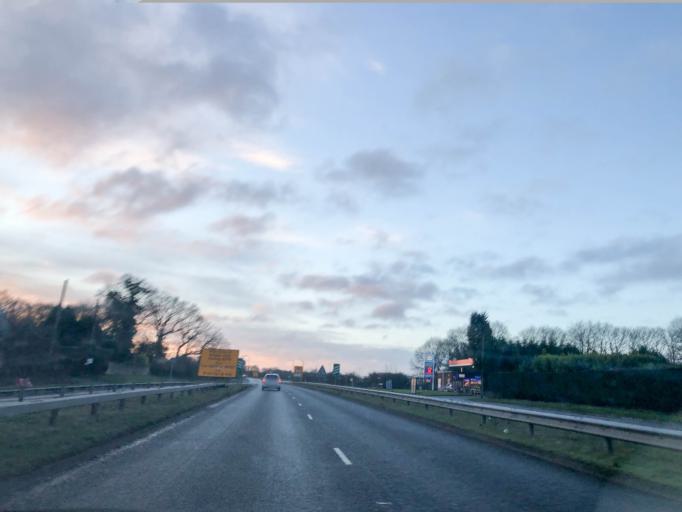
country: GB
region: England
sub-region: Solihull
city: Tidbury Green
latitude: 52.3593
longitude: -1.8886
